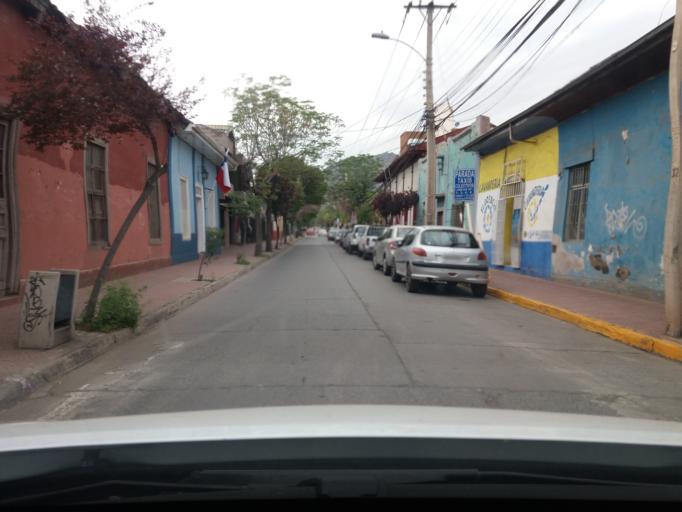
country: CL
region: Valparaiso
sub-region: Provincia de Los Andes
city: Los Andes
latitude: -32.8330
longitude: -70.6027
